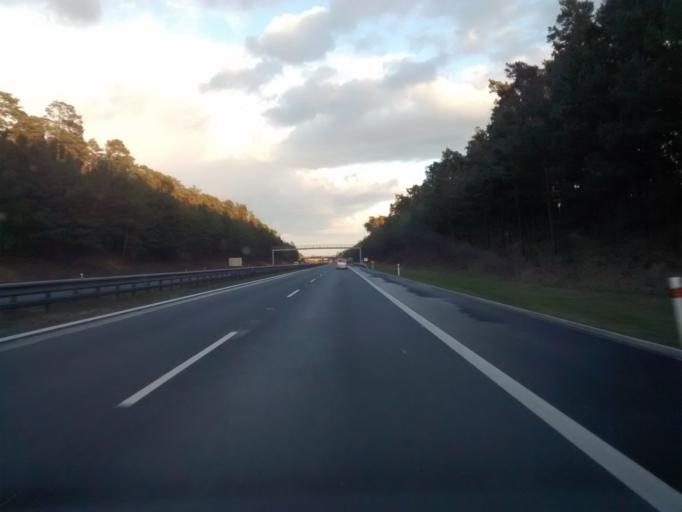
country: CZ
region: Central Bohemia
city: Poricany
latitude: 50.1219
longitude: 14.9328
